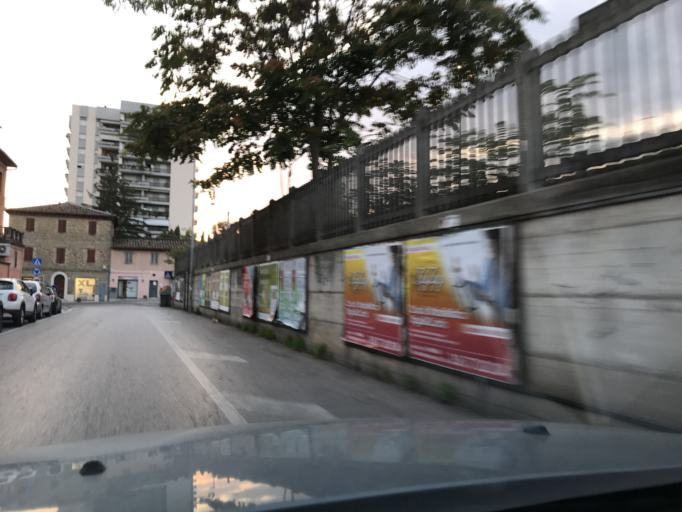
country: IT
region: Umbria
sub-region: Provincia di Perugia
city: Ponte Felcino
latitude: 43.0911
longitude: 12.4368
